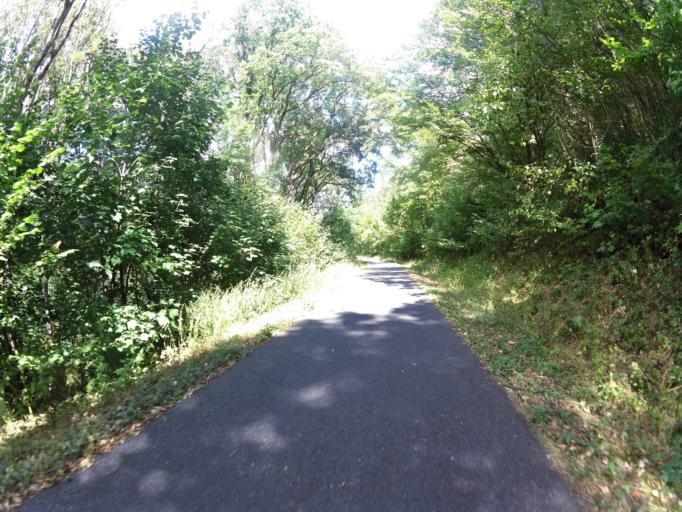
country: DE
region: Bavaria
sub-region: Regierungsbezirk Unterfranken
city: Ochsenfurt
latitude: 49.6586
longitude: 10.0343
